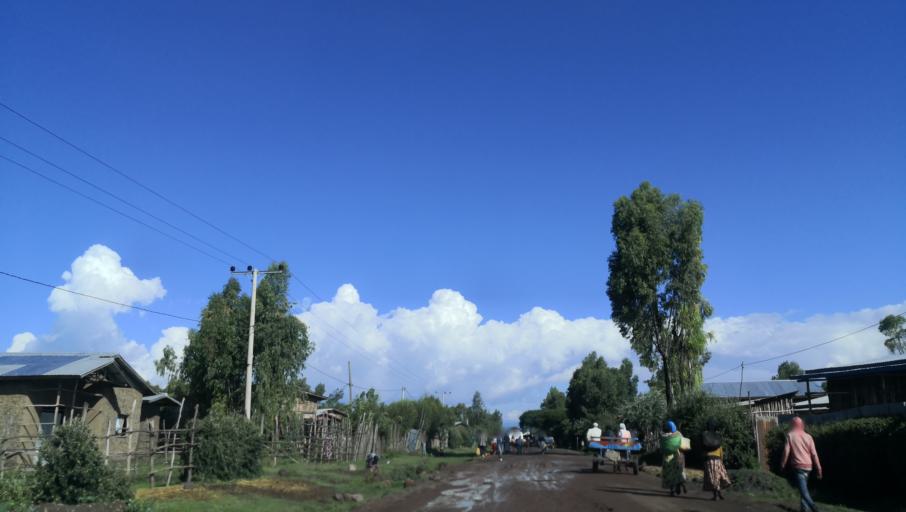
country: ET
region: Oromiya
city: Tulu Bolo
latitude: 8.6452
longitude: 38.2211
